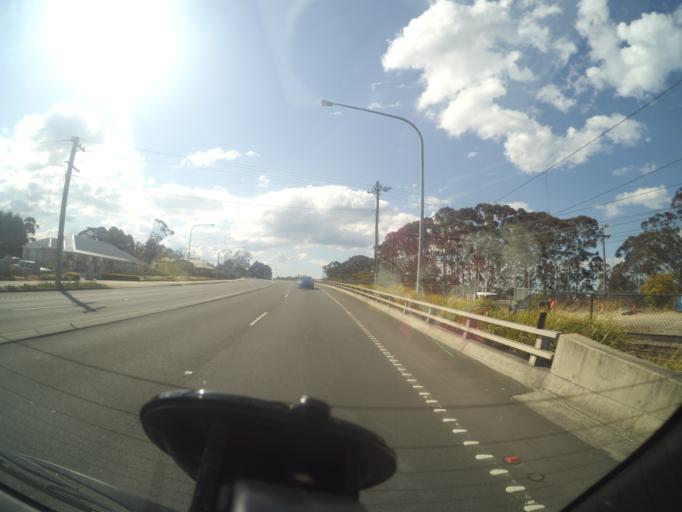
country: AU
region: New South Wales
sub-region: Blue Mountains Municipality
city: Katoomba
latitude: -33.7092
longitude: 150.3164
